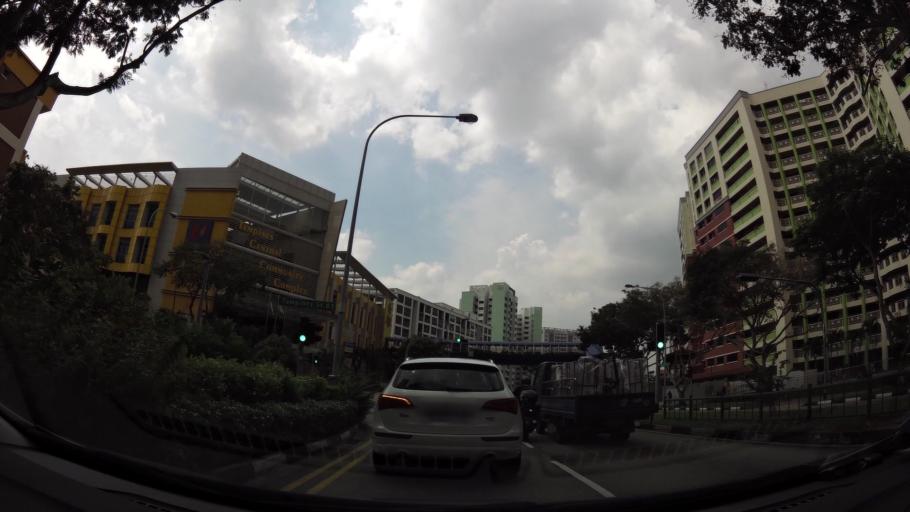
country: SG
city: Singapore
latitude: 1.3557
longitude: 103.9352
